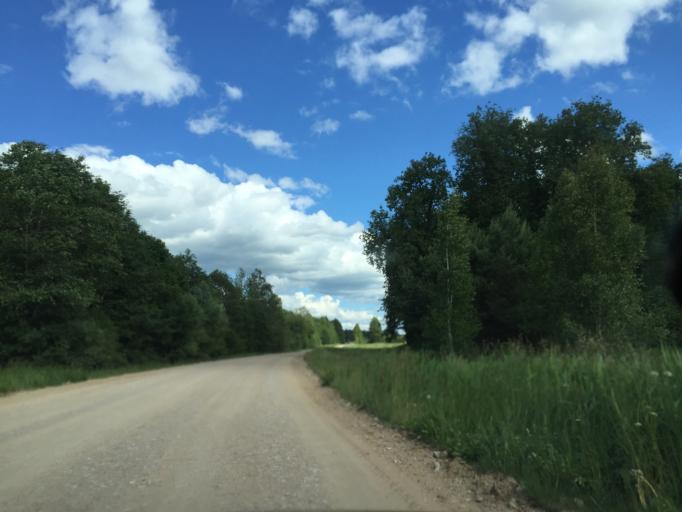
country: LV
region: Vecumnieki
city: Vecumnieki
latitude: 56.4029
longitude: 24.5476
